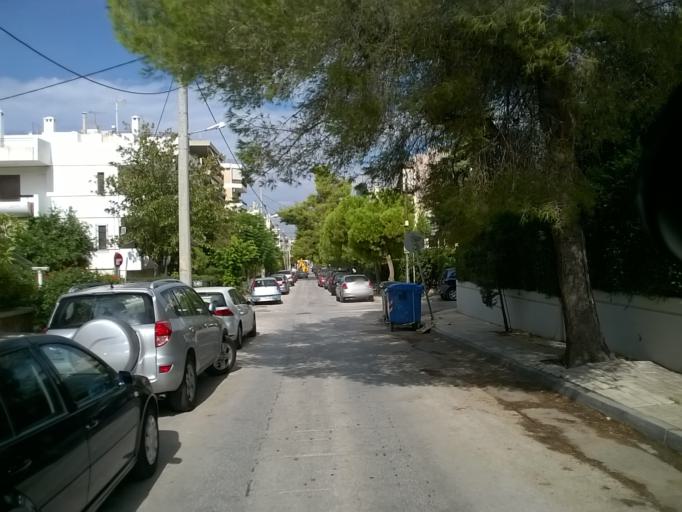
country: GR
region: Attica
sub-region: Nomarchia Athinas
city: Argyroupoli
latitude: 37.8862
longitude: 23.7637
